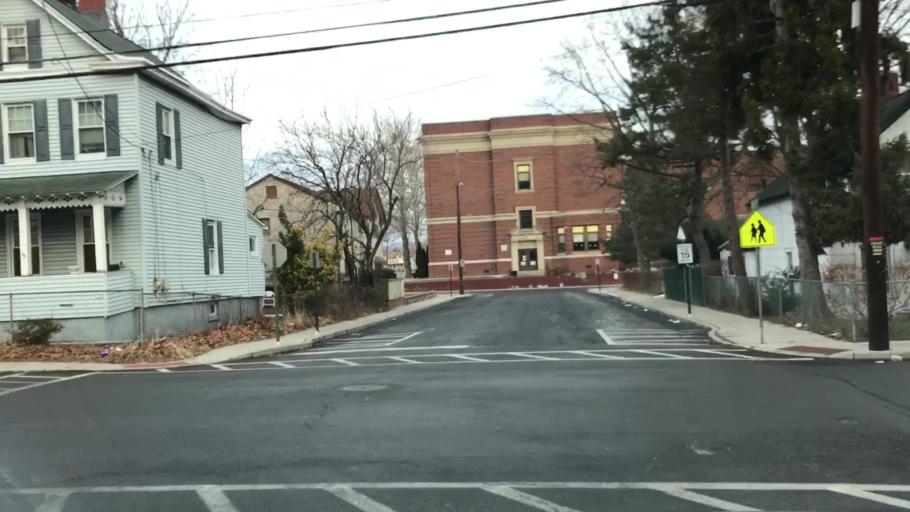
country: US
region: New York
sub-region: Rockland County
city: Haverstraw
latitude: 41.1971
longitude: -73.9666
